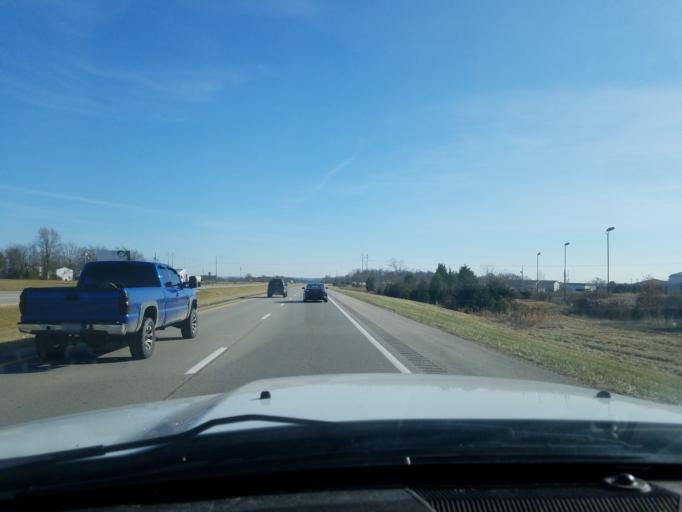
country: US
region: Ohio
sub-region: Adams County
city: Winchester
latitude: 38.9320
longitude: -83.5678
